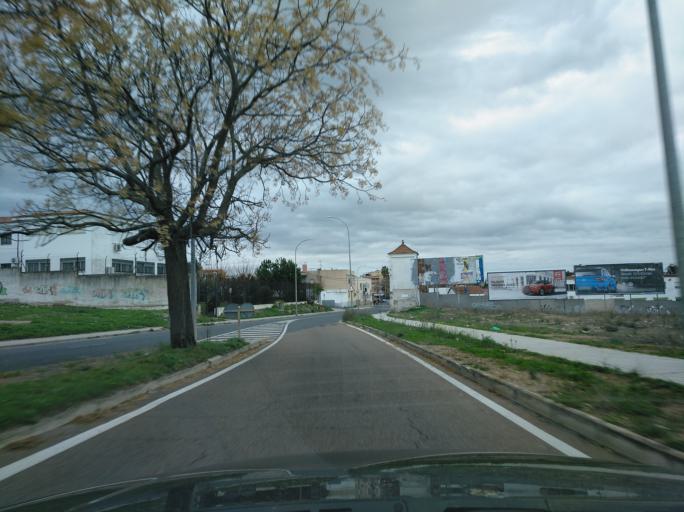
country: ES
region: Extremadura
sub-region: Provincia de Badajoz
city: Badajoz
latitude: 38.8945
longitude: -6.9829
